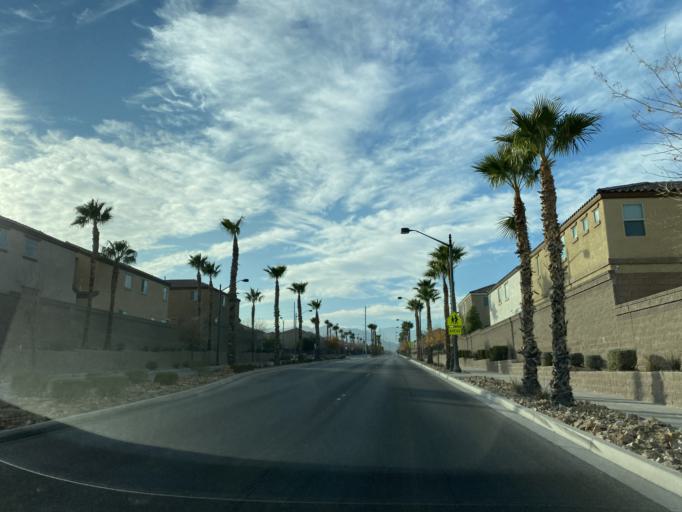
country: US
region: Nevada
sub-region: Clark County
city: Summerlin South
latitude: 36.2992
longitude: -115.2926
